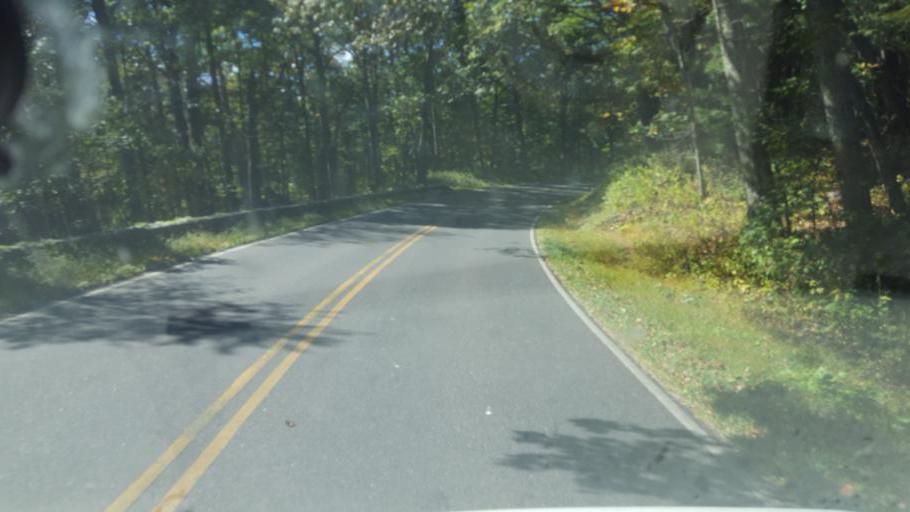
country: US
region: Virginia
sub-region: Greene County
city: Stanardsville
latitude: 38.3871
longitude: -78.5086
